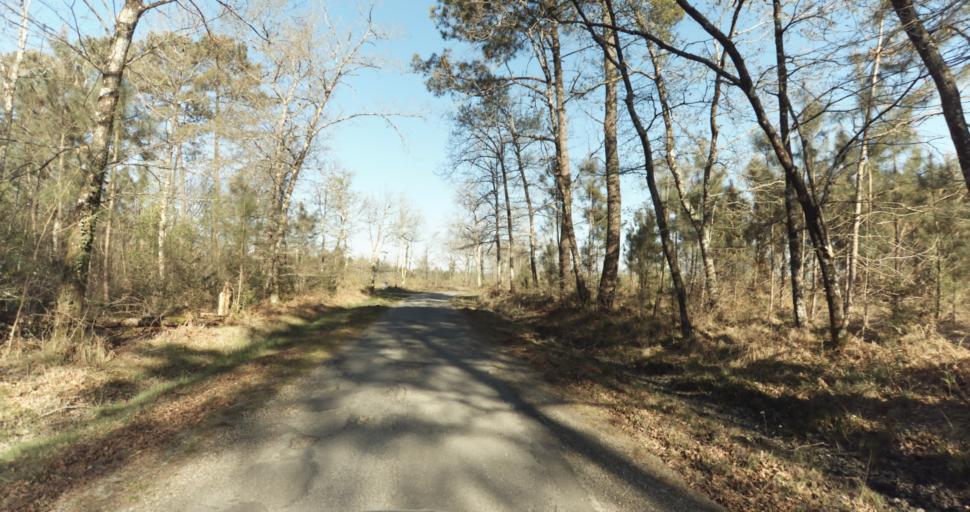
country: FR
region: Aquitaine
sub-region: Departement de la Gironde
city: Martignas-sur-Jalle
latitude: 44.8071
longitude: -0.8479
